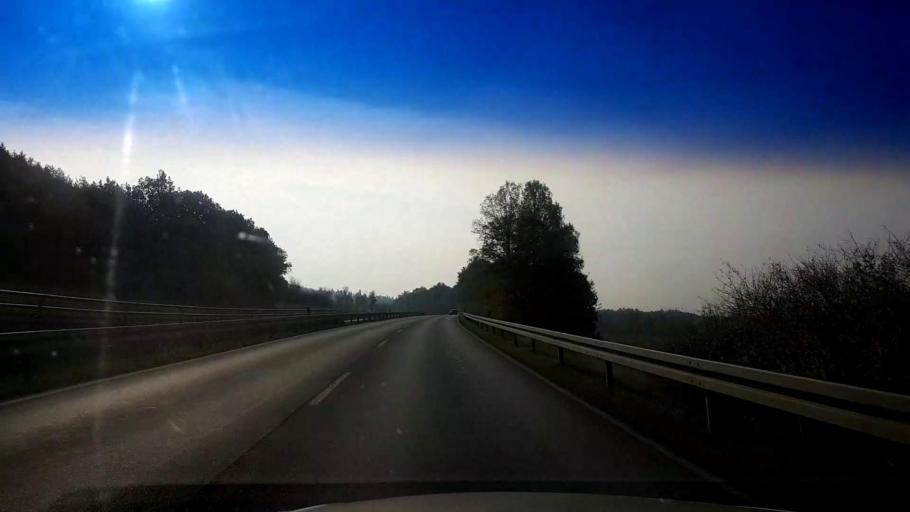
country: DE
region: Bavaria
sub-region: Upper Franconia
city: Neuenmarkt
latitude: 50.0964
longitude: 11.6069
